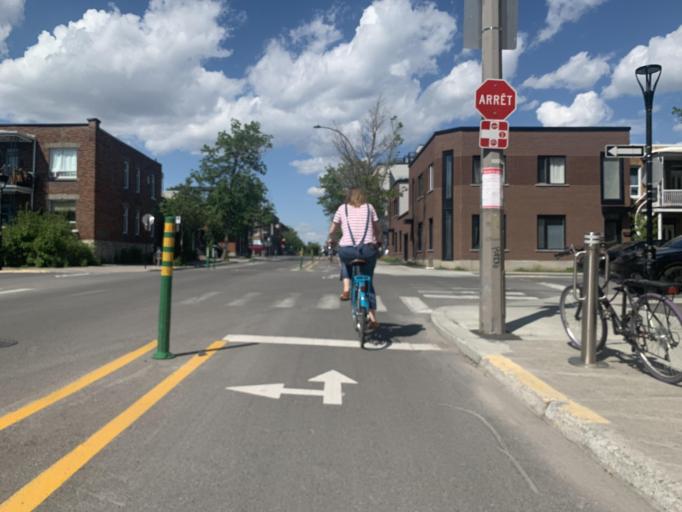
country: CA
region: Quebec
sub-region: Montreal
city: Montreal
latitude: 45.5432
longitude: -73.5918
